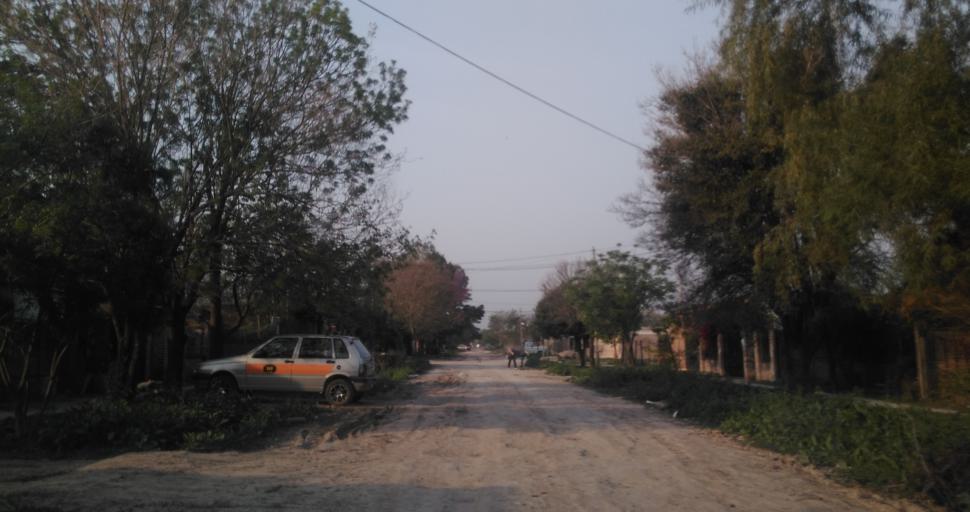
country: AR
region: Chaco
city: Resistencia
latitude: -27.4748
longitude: -59.0111
